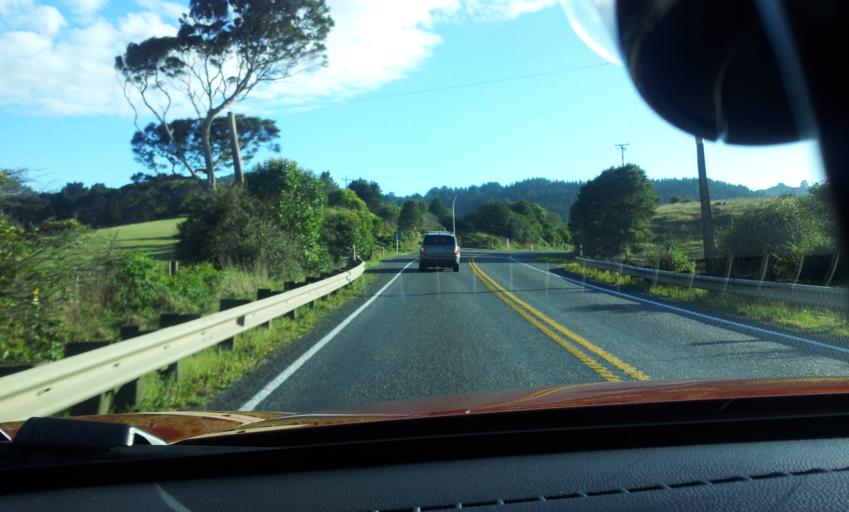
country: NZ
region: Auckland
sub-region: Auckland
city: Pukekohe East
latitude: -37.2205
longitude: 175.0456
